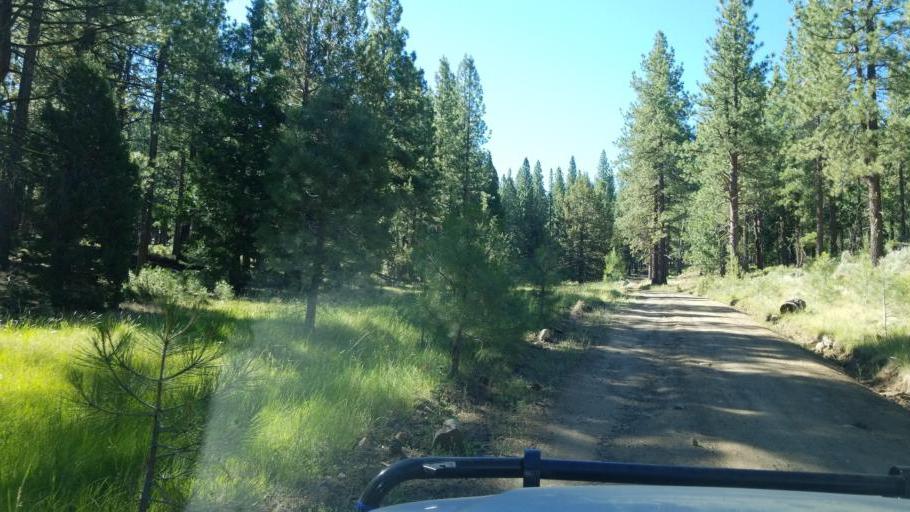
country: US
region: California
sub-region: Lassen County
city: Susanville
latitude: 40.5796
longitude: -120.7423
